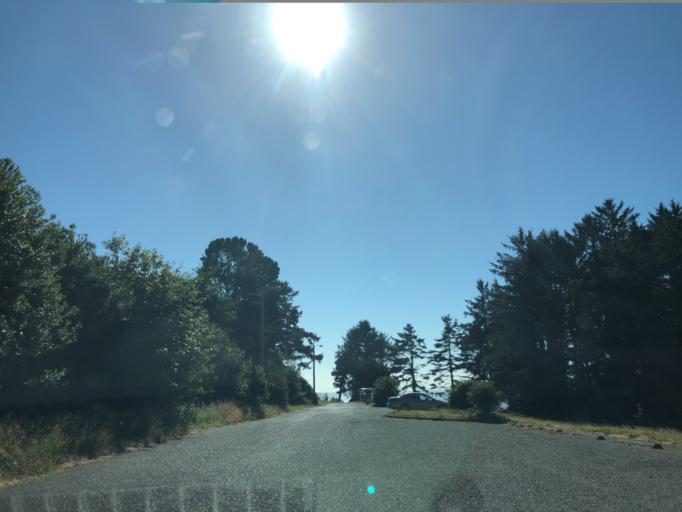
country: US
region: California
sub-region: Humboldt County
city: Westhaven-Moonstone
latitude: 41.0610
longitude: -124.1448
